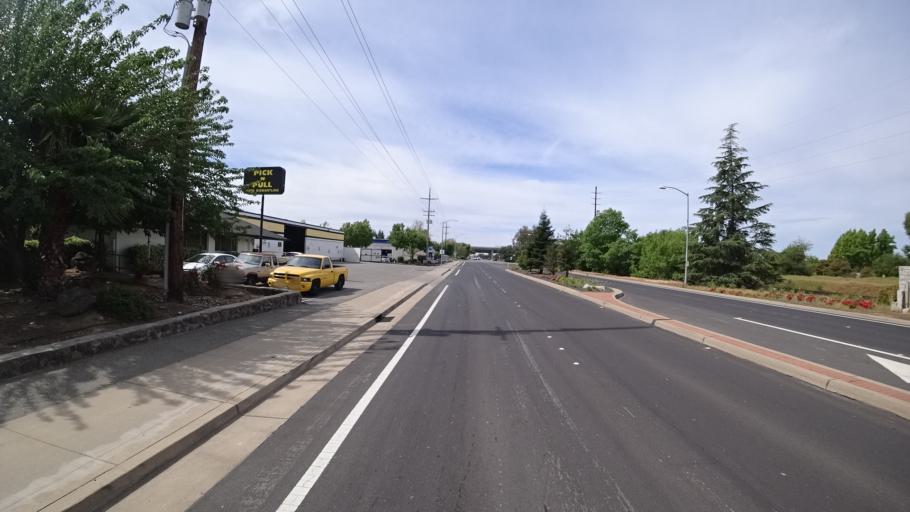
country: US
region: California
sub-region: Placer County
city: Rocklin
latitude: 38.7749
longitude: -121.2491
